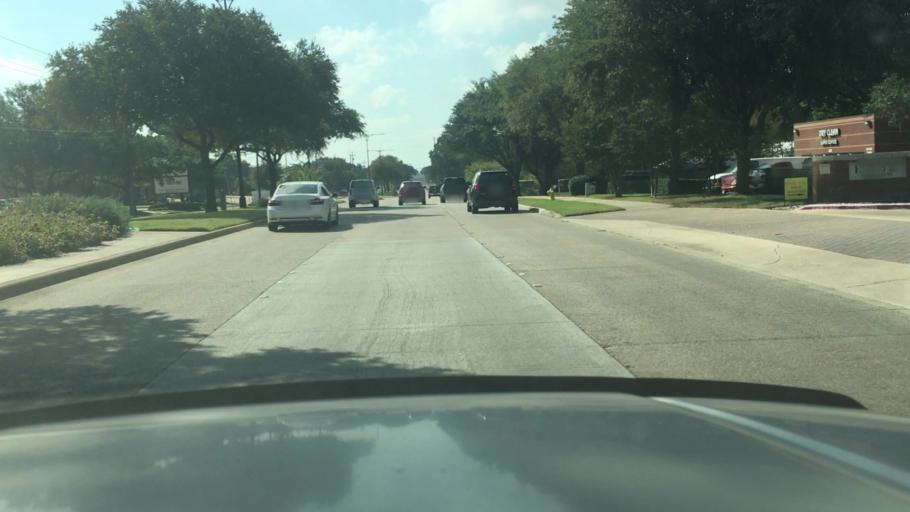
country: US
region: Texas
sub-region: Dallas County
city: Coppell
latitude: 32.9595
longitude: -96.9936
